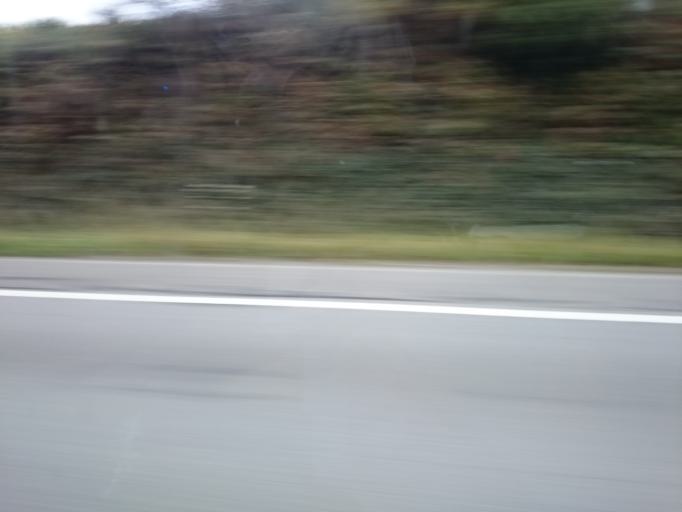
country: FR
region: Brittany
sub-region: Departement du Morbihan
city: Hennebont
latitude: 47.7889
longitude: -3.2539
